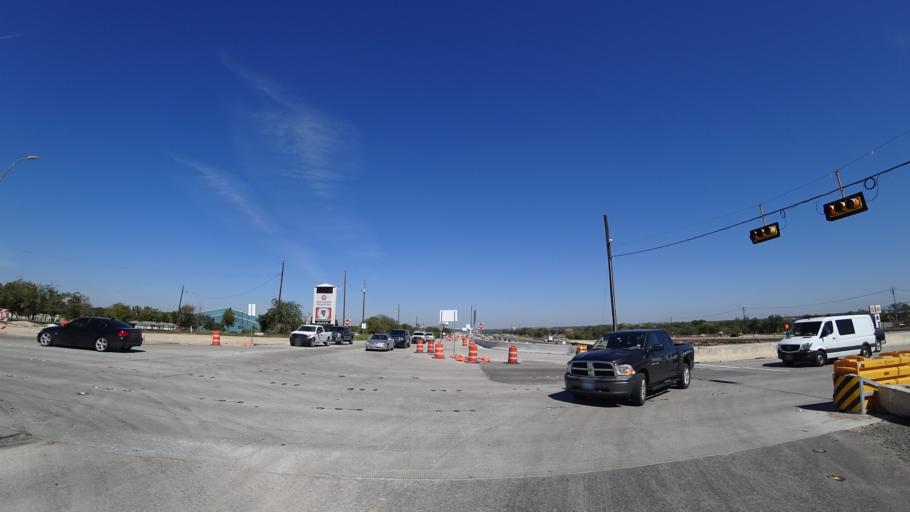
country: US
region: Texas
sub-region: Travis County
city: Austin
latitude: 30.2859
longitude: -97.6659
